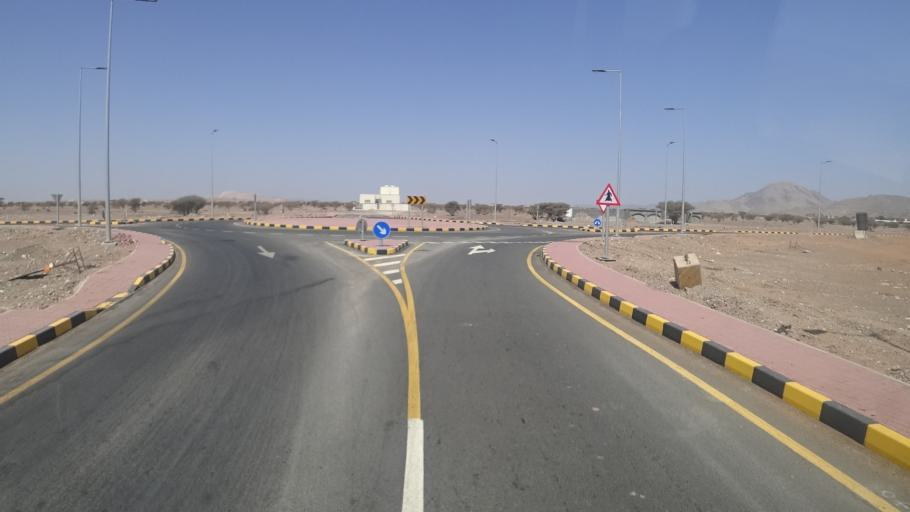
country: OM
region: Ash Sharqiyah
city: Badiyah
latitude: 22.5024
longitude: 58.9456
